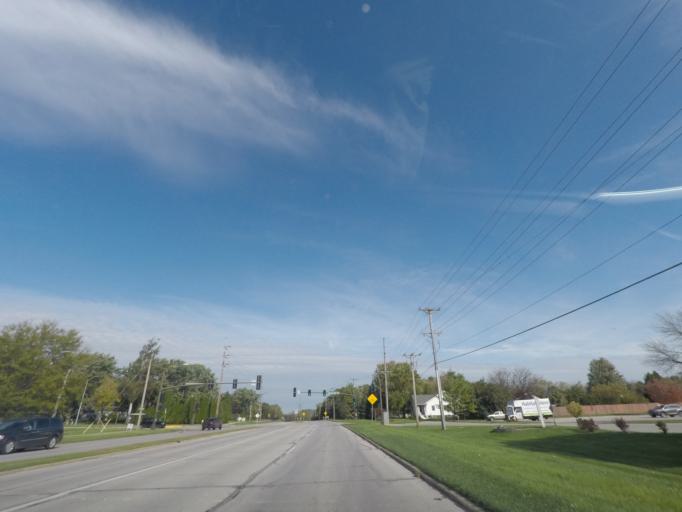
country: US
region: Iowa
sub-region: Story County
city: Ames
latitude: 42.0553
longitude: -93.6205
